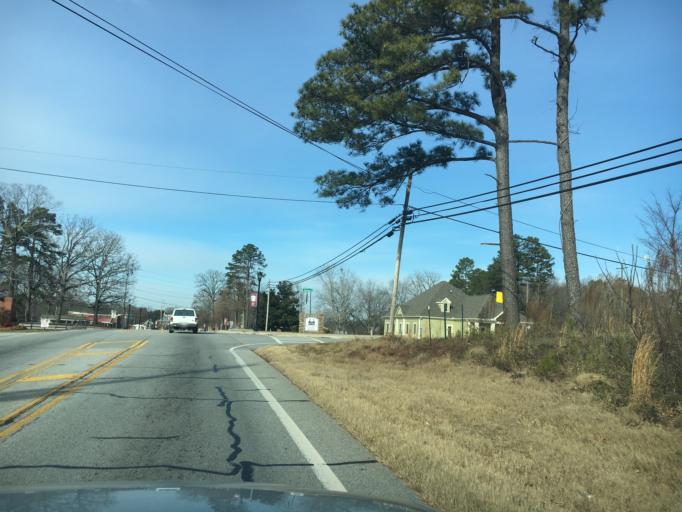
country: US
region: Georgia
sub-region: Jackson County
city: Braselton
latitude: 34.1047
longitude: -83.7619
